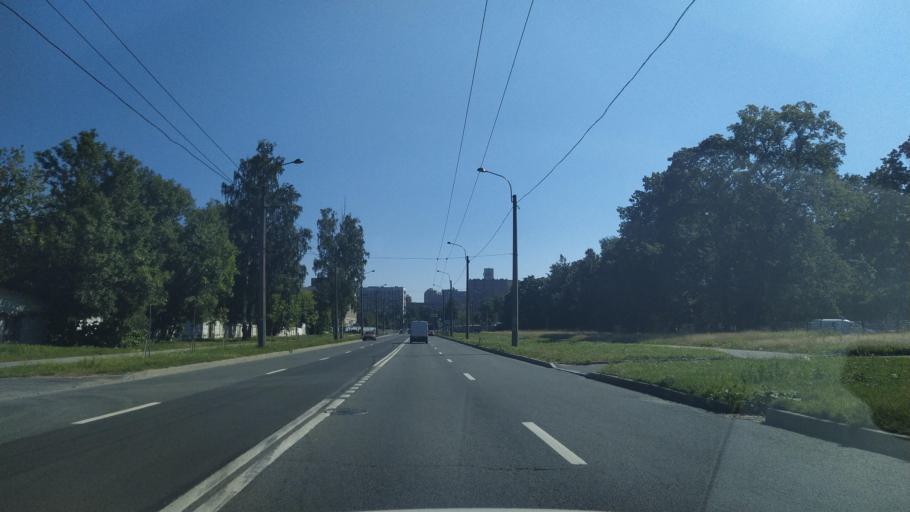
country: RU
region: Leningrad
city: Kalininskiy
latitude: 60.0082
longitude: 30.3816
